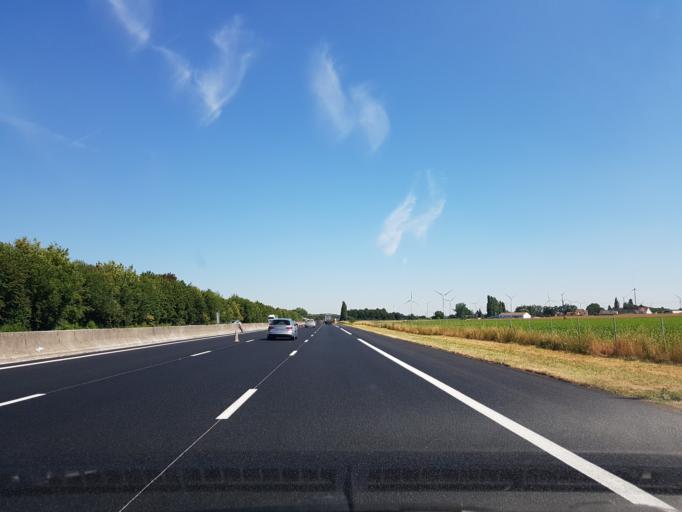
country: FR
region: Picardie
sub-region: Departement de la Somme
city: Roye
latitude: 49.6405
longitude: 2.7586
